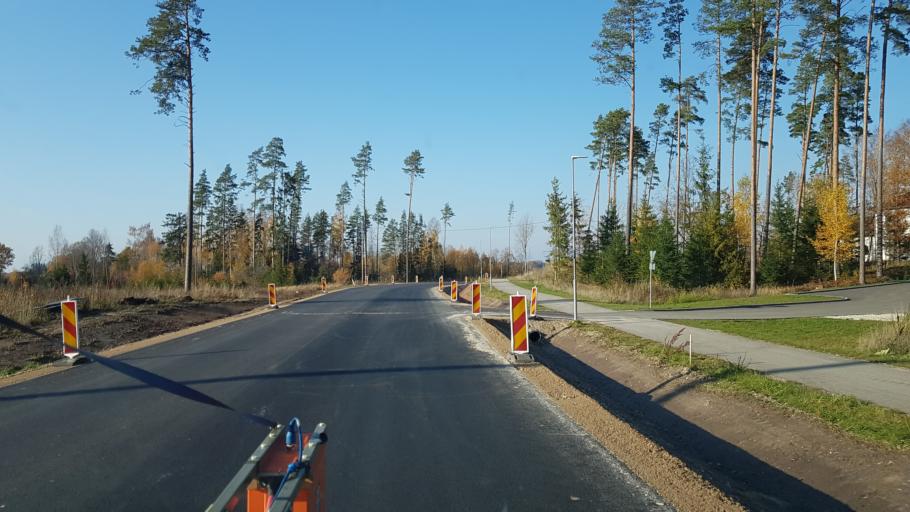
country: EE
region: Vorumaa
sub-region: Antsla vald
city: Vana-Antsla
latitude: 57.8328
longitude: 26.5092
